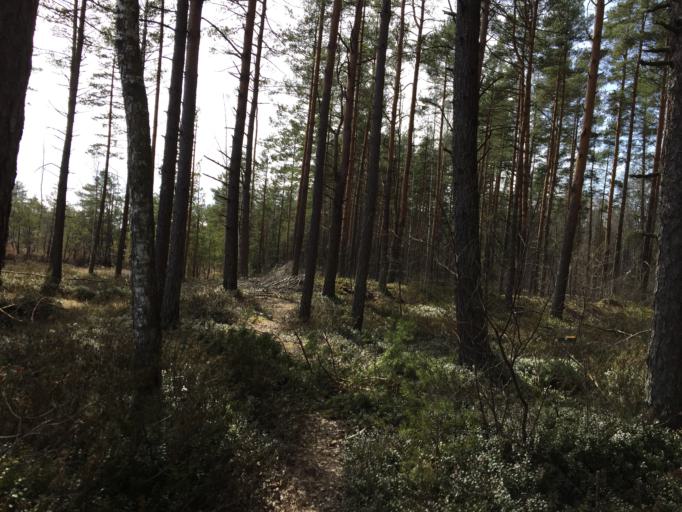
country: LV
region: Salaspils
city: Salaspils
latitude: 56.8831
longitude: 24.3620
